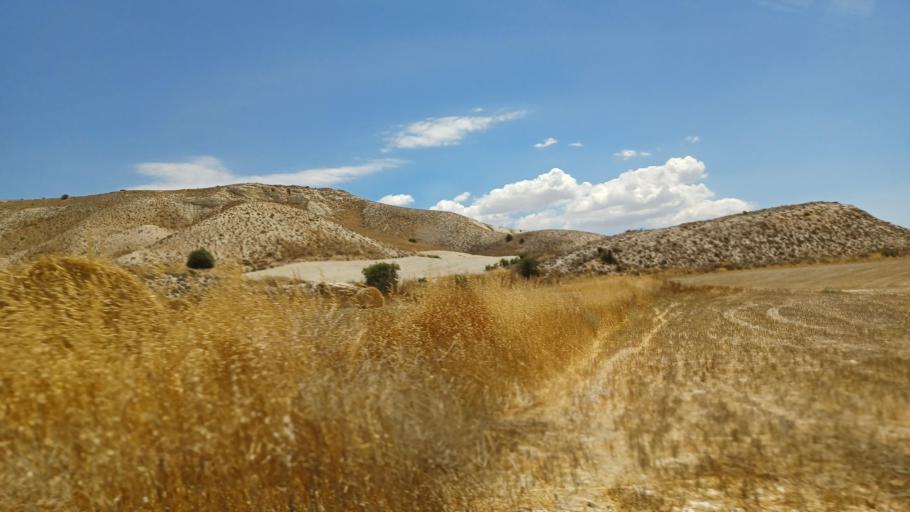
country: CY
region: Larnaka
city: Troulloi
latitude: 35.0391
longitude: 33.6259
